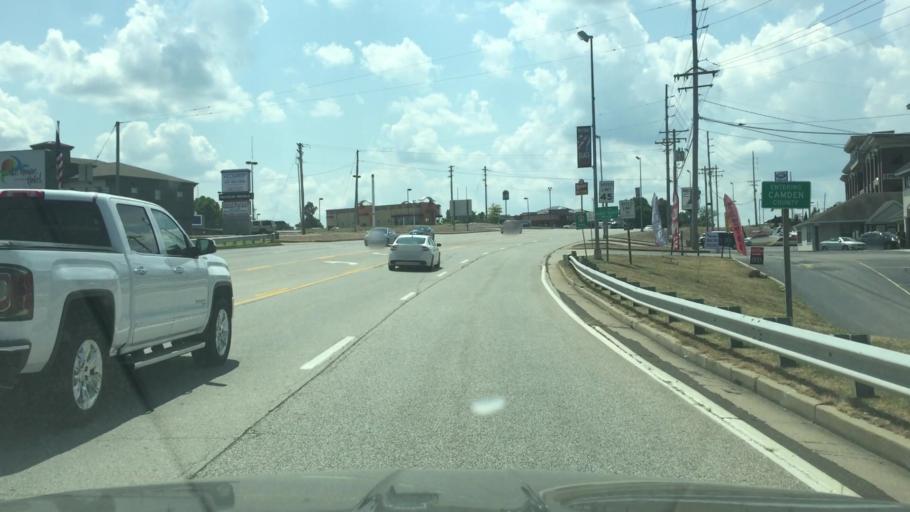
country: US
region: Missouri
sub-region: Miller County
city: Lake Ozark
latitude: 38.1711
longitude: -92.6124
